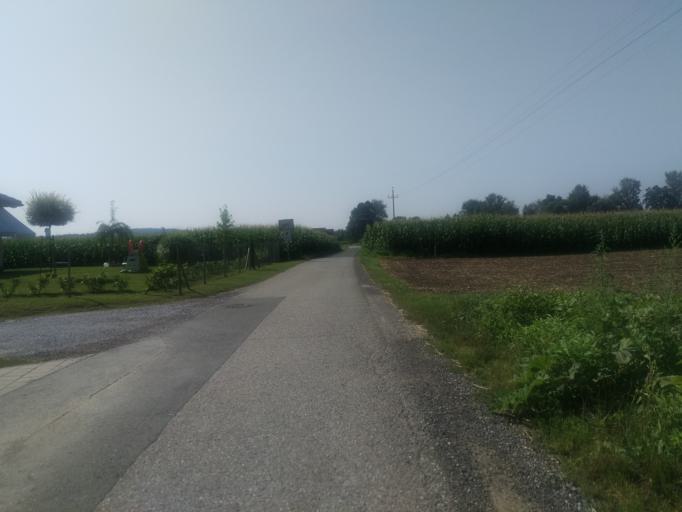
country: AT
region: Styria
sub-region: Politischer Bezirk Graz-Umgebung
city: Gossendorf
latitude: 46.9898
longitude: 15.4872
